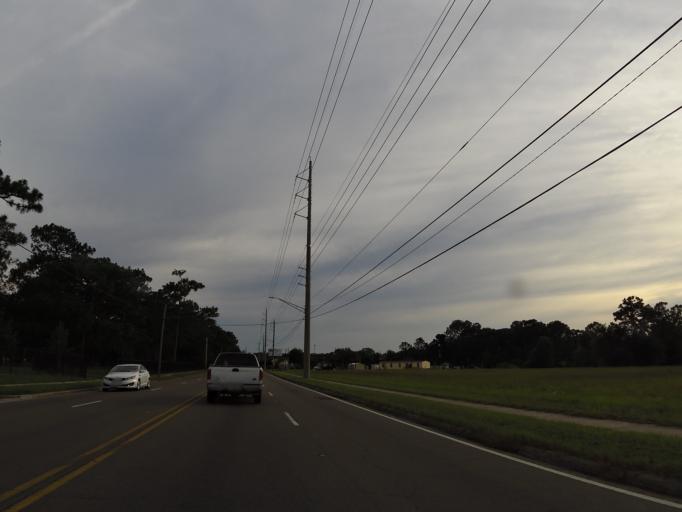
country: US
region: Florida
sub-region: Duval County
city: Jacksonville
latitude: 30.3960
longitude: -81.7271
